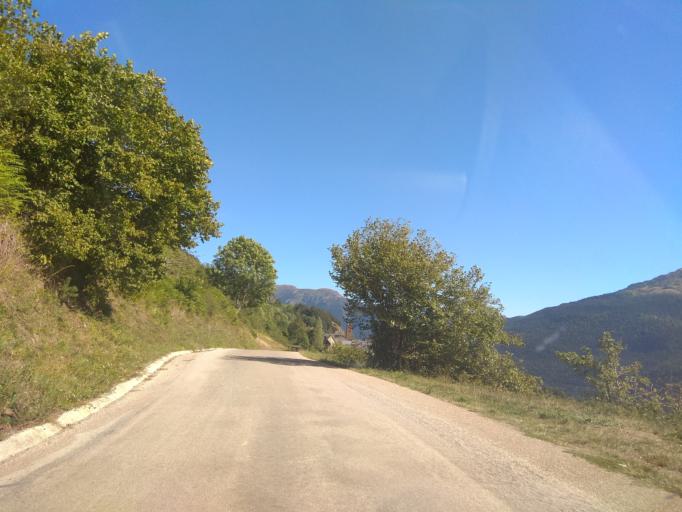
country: ES
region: Catalonia
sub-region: Provincia de Lleida
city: Les
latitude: 42.7493
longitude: 0.7213
